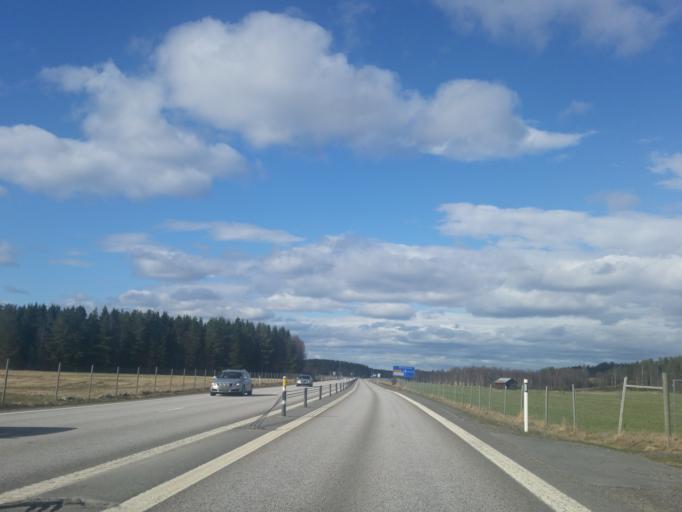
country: SE
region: Vaesterbotten
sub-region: Robertsfors Kommun
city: Robertsfors
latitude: 64.1337
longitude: 20.8924
